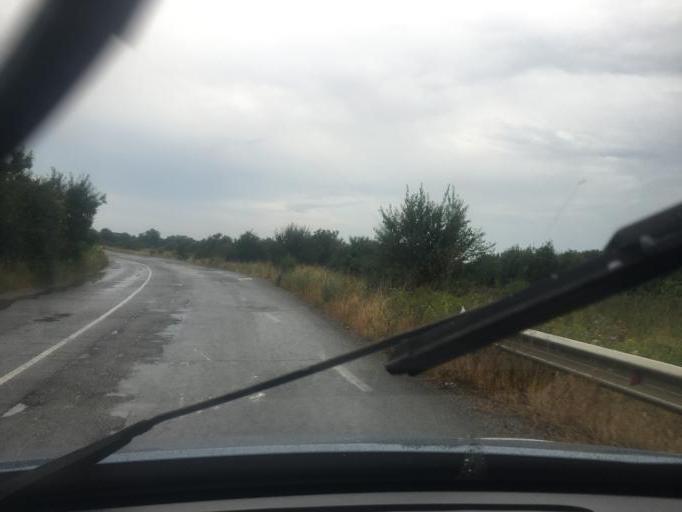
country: BG
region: Burgas
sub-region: Obshtina Burgas
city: Burgas
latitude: 42.5563
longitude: 27.4906
